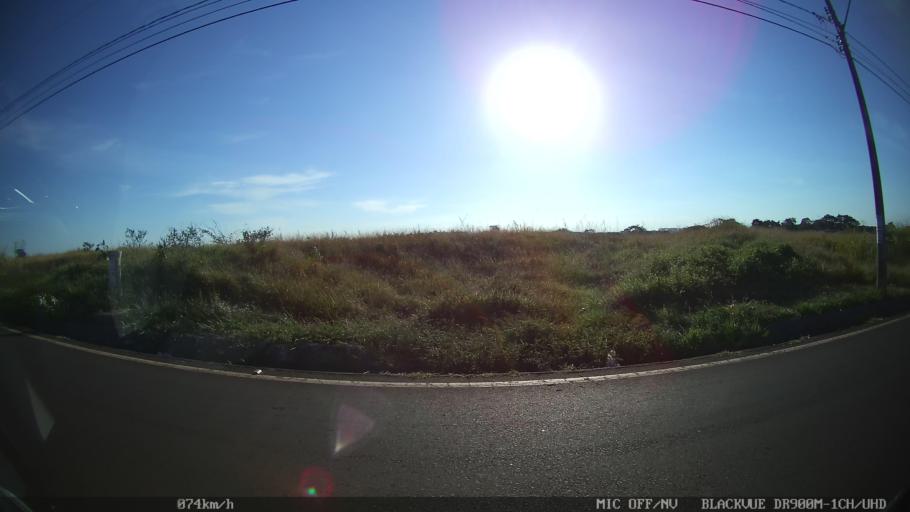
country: BR
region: Sao Paulo
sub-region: Franca
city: Franca
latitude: -20.5066
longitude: -47.3719
